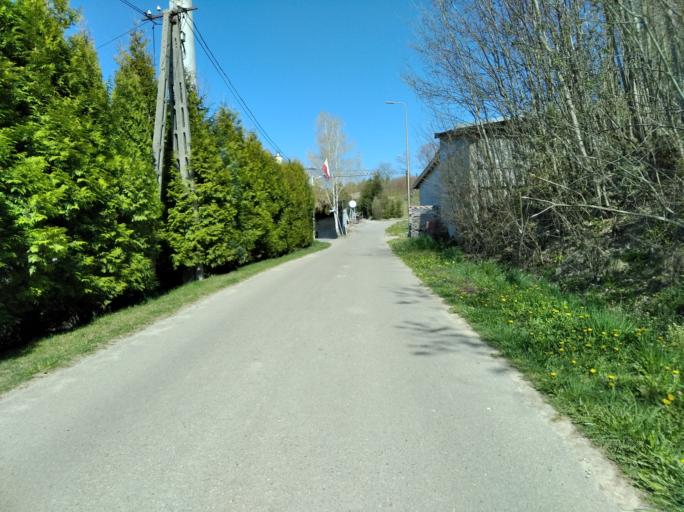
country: PL
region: Subcarpathian Voivodeship
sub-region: Powiat strzyzowski
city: Wisniowa
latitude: 49.8986
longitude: 21.6626
